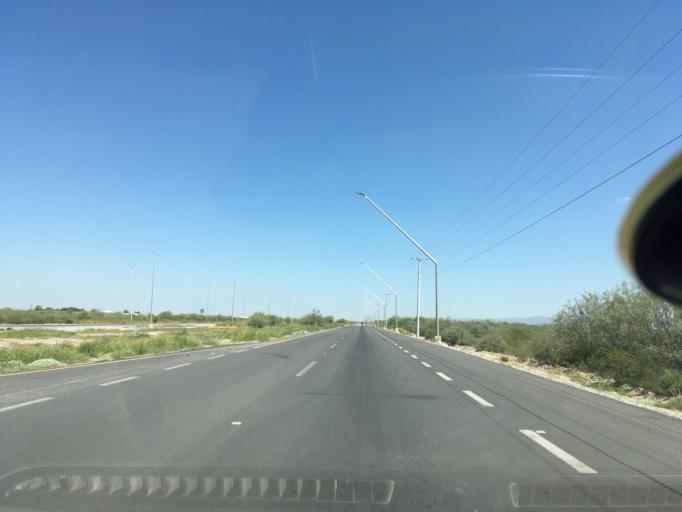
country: MX
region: Coahuila
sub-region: Torreon
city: Fraccionamiento la Noria
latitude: 25.4639
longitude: -103.3231
